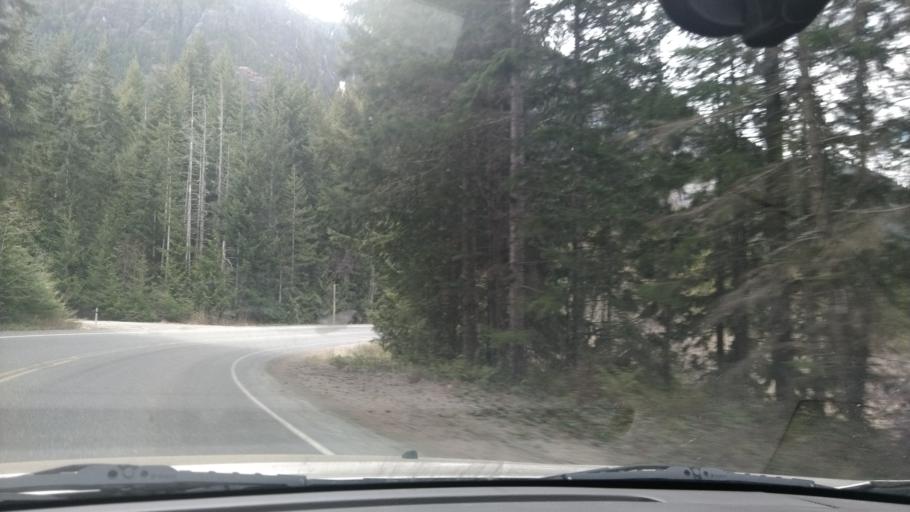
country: CA
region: British Columbia
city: Campbell River
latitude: 49.8452
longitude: -125.6406
